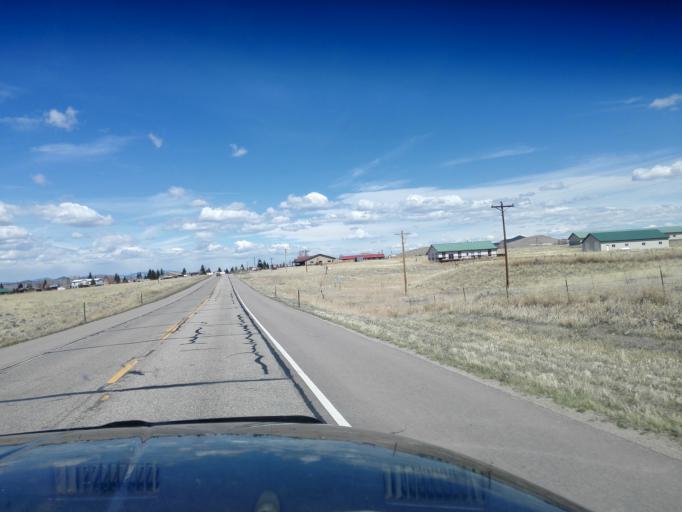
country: US
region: Colorado
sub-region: Custer County
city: Westcliffe
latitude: 38.1264
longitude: -105.4629
